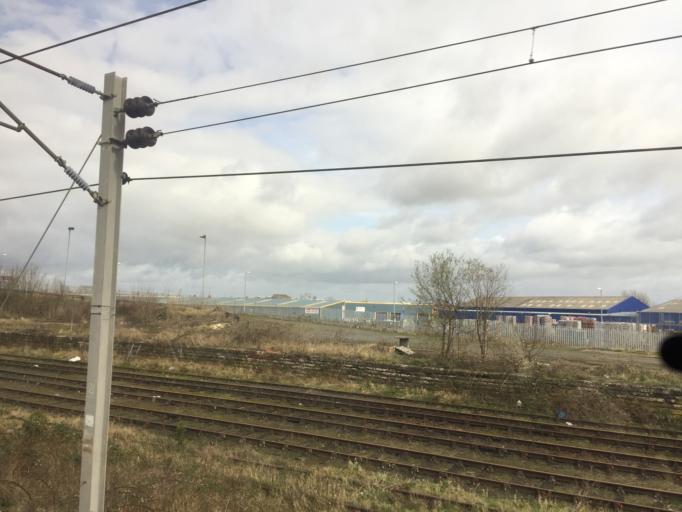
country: GB
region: England
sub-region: Cumbria
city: Carlisle
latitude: 54.8844
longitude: -2.9251
